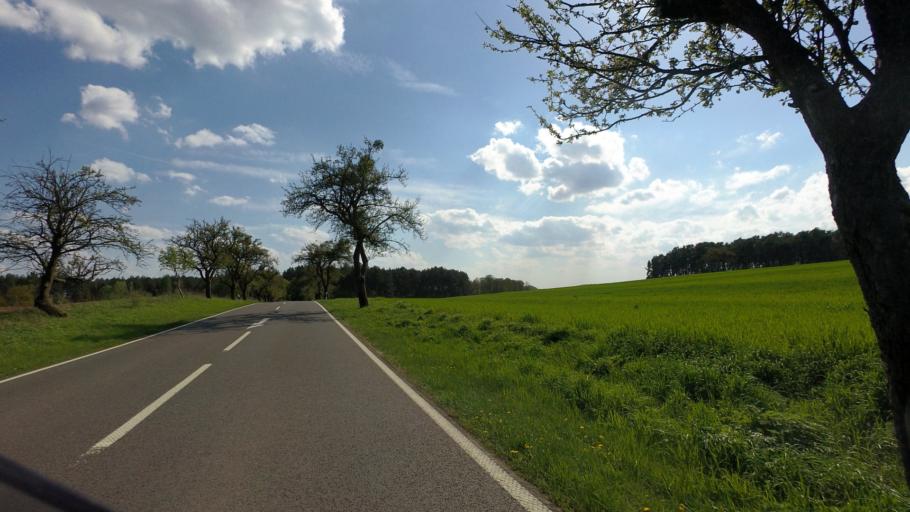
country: DE
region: Brandenburg
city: Templin
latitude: 53.1007
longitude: 13.5006
